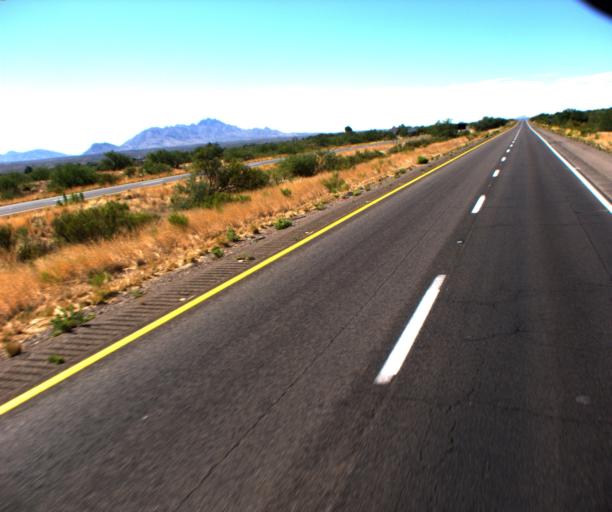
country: US
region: Arizona
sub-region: Santa Cruz County
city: Tubac
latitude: 31.6430
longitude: -111.0580
